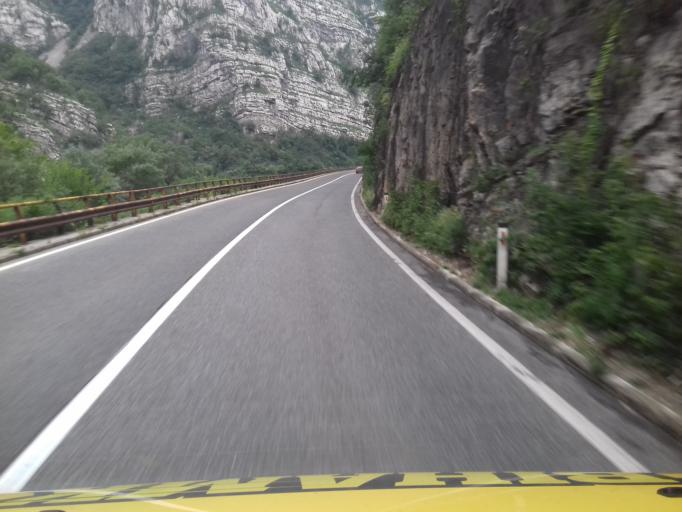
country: BA
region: Federation of Bosnia and Herzegovina
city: Jablanica
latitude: 43.6083
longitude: 17.7416
